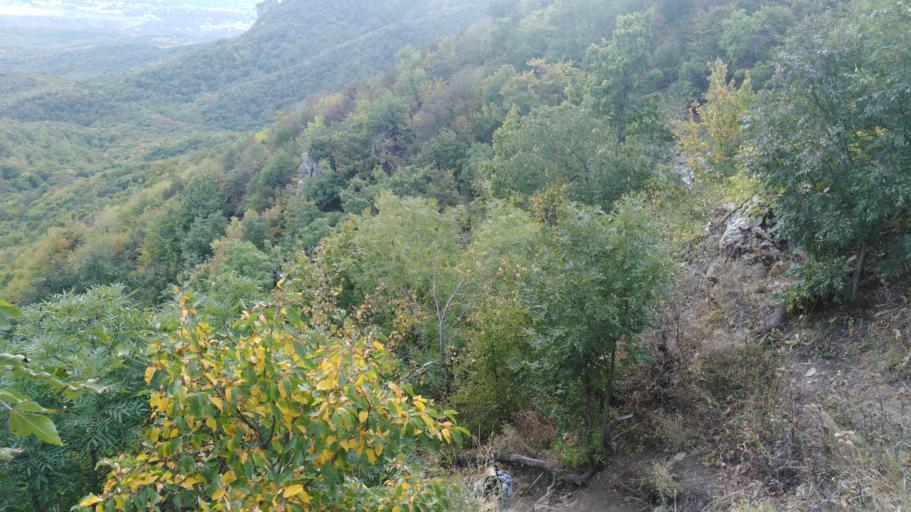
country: RU
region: Stavropol'skiy
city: Zheleznovodsk
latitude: 44.0964
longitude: 43.0274
